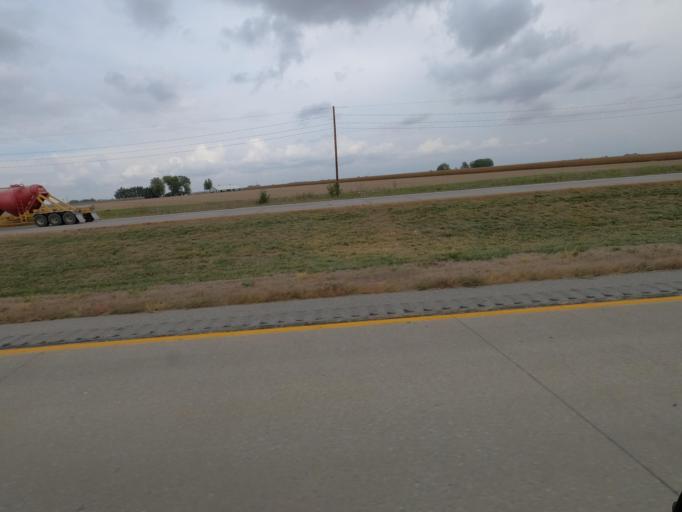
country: US
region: Iowa
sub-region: Jasper County
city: Prairie City
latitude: 41.5768
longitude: -93.1760
